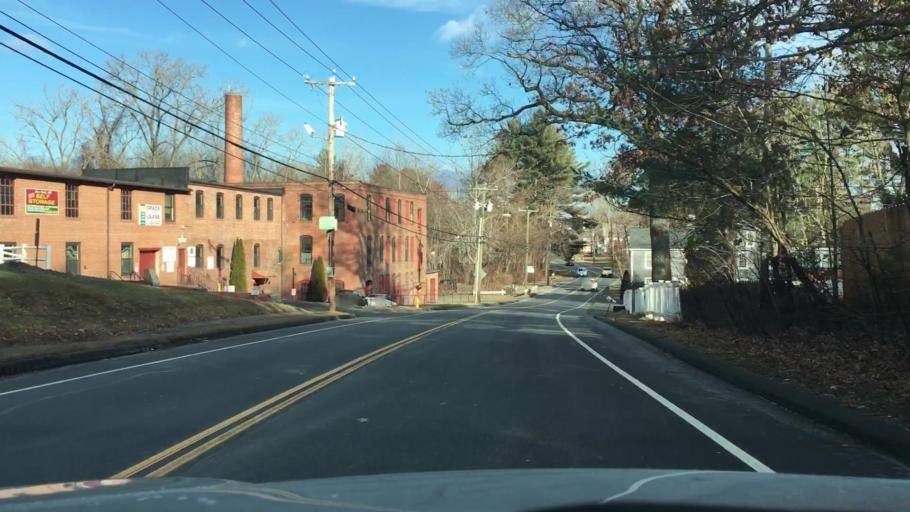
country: US
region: Massachusetts
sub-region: Hampden County
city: Agawam
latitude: 42.0653
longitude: -72.6235
